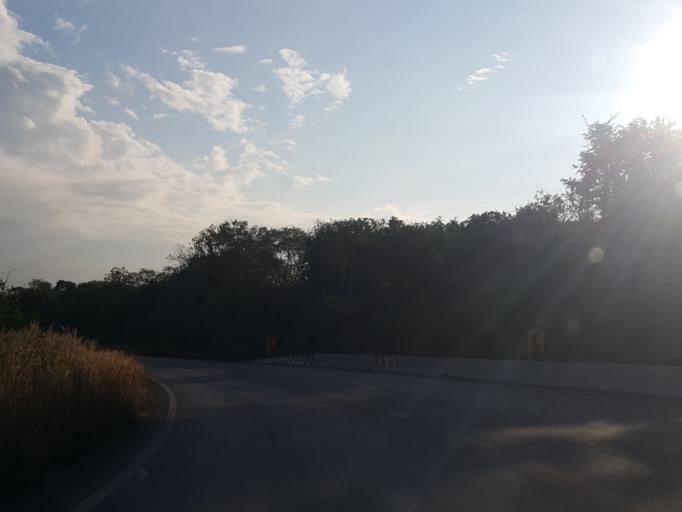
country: TH
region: Lampang
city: Lampang
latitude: 18.4318
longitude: 99.5423
